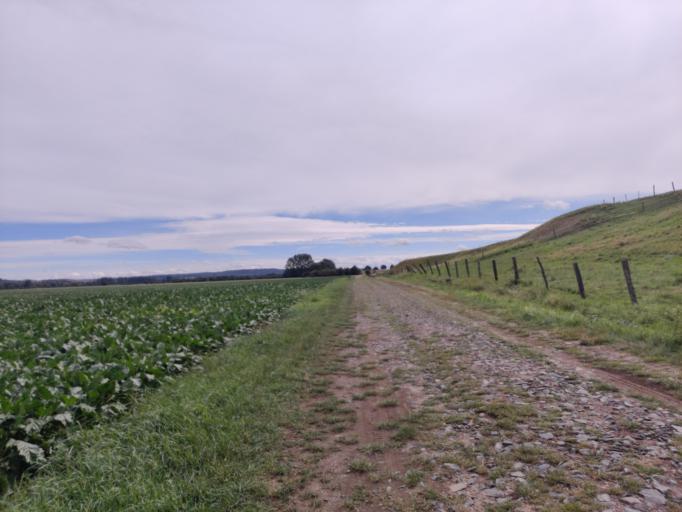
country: DE
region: Lower Saxony
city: Alt Wallmoden
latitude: 52.0127
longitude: 10.3476
